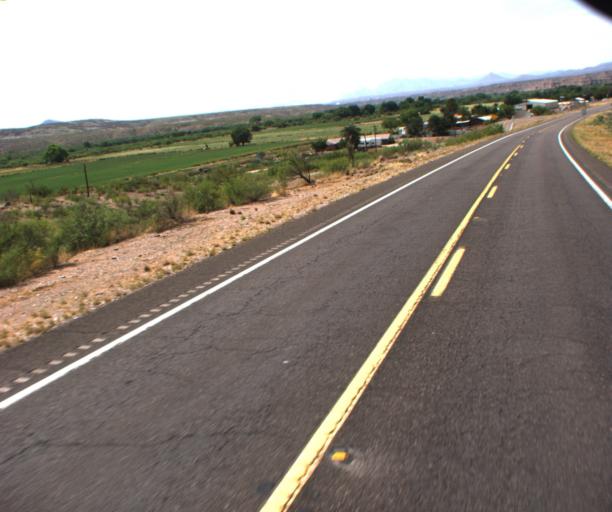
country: US
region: Arizona
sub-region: Greenlee County
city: Clifton
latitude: 32.9015
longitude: -109.1964
